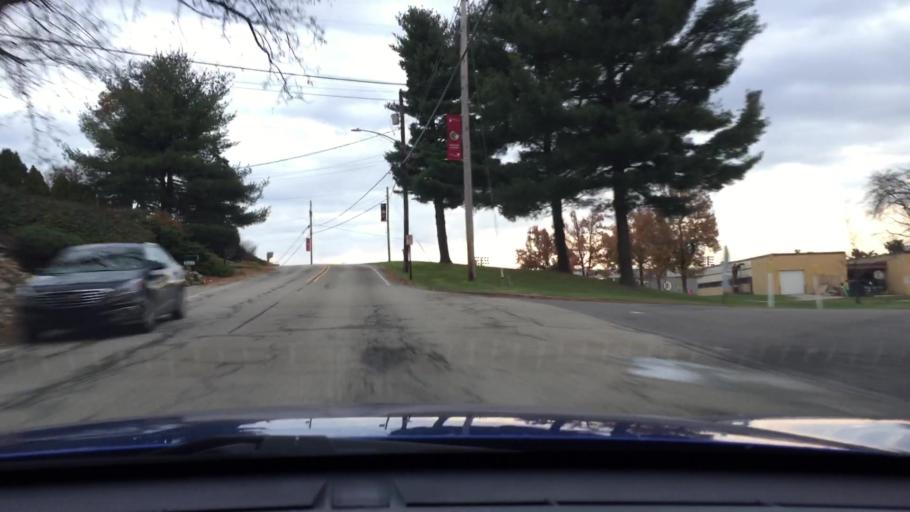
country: US
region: Pennsylvania
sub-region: Allegheny County
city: Elizabeth
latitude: 40.2564
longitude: -79.8572
